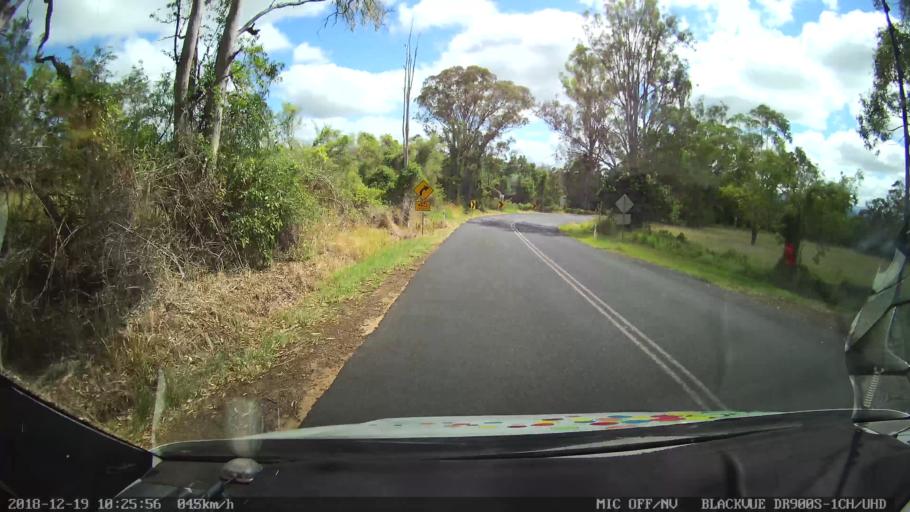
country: AU
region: New South Wales
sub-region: Lismore Municipality
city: Larnook
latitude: -28.5935
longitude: 153.0883
